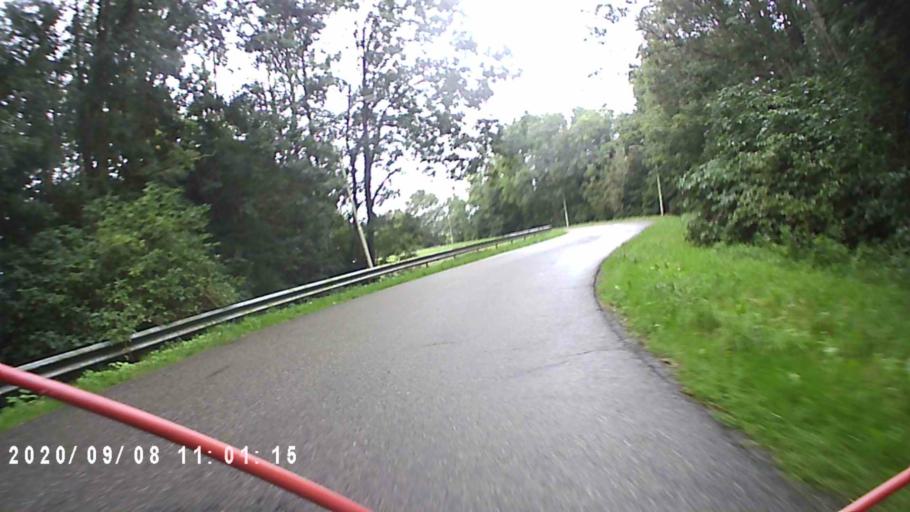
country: NL
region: Groningen
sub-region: Gemeente Haren
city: Haren
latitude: 53.1993
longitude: 6.6651
